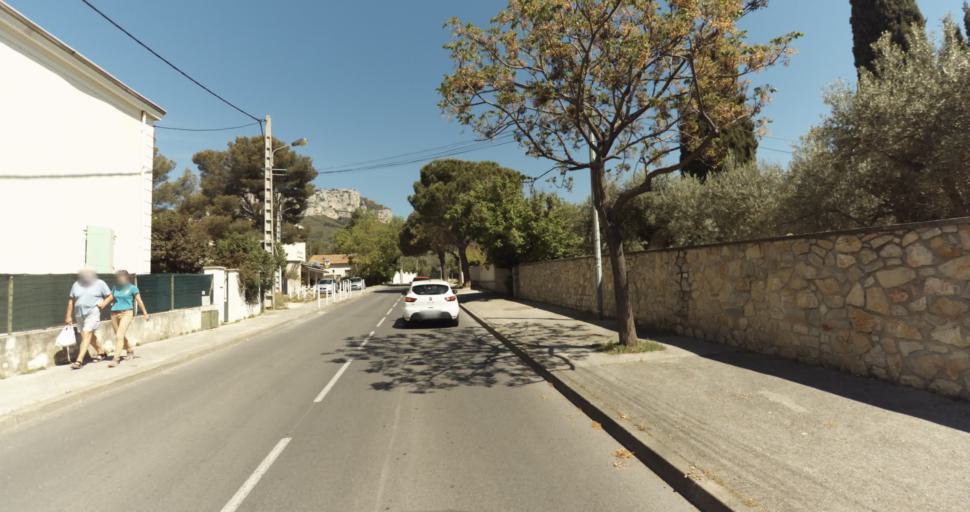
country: FR
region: Provence-Alpes-Cote d'Azur
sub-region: Departement du Var
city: Le Revest-les-Eaux
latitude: 43.1447
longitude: 5.9017
